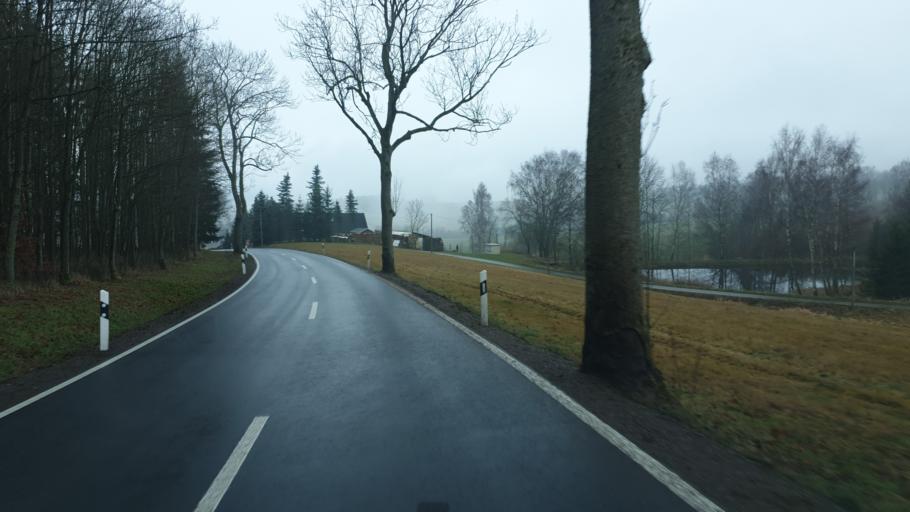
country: DE
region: Saxony
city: Neuhausen
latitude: 50.6905
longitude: 13.4601
